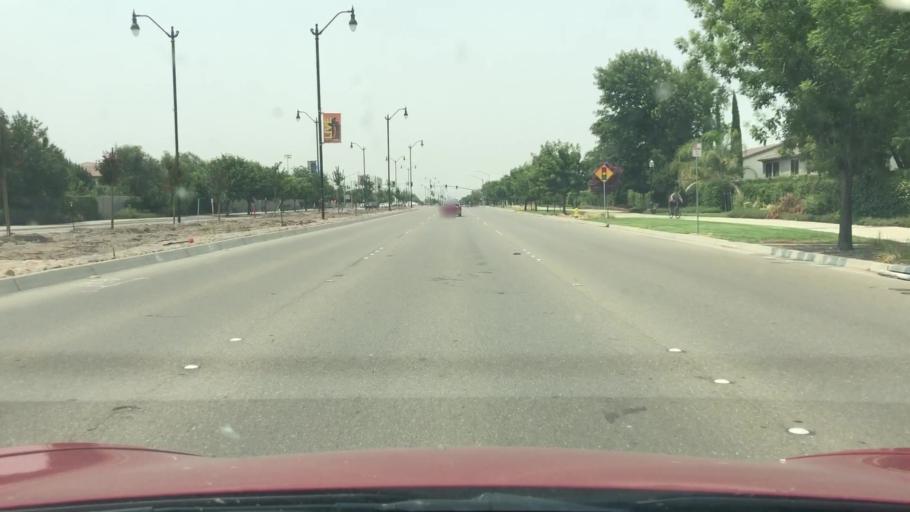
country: US
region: California
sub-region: San Joaquin County
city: Tracy
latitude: 37.7394
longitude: -121.4612
